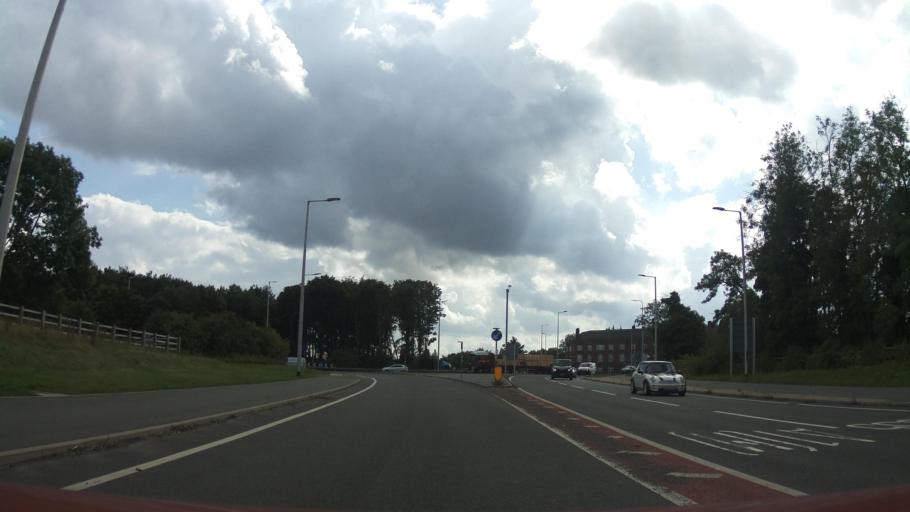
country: GB
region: England
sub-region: North Yorkshire
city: Catterick
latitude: 54.4444
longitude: -1.6704
